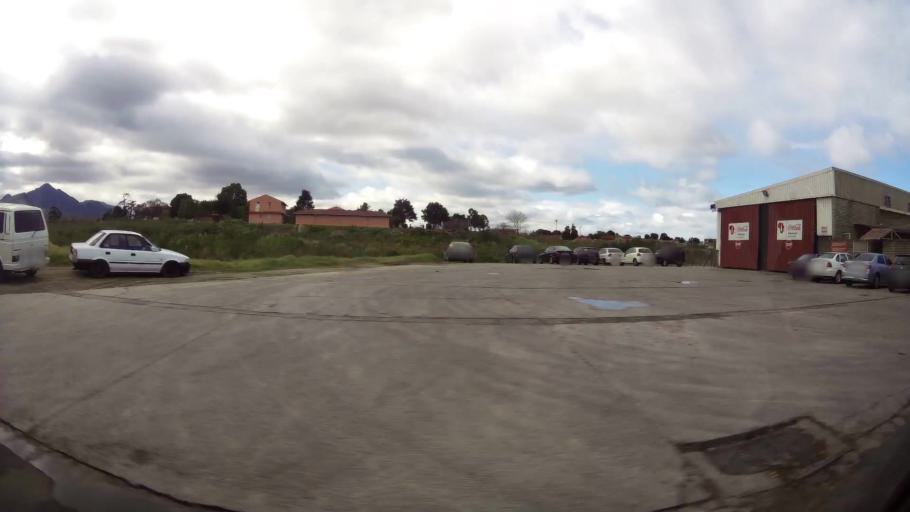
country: ZA
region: Western Cape
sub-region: Eden District Municipality
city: George
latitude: -33.9689
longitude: 22.4733
